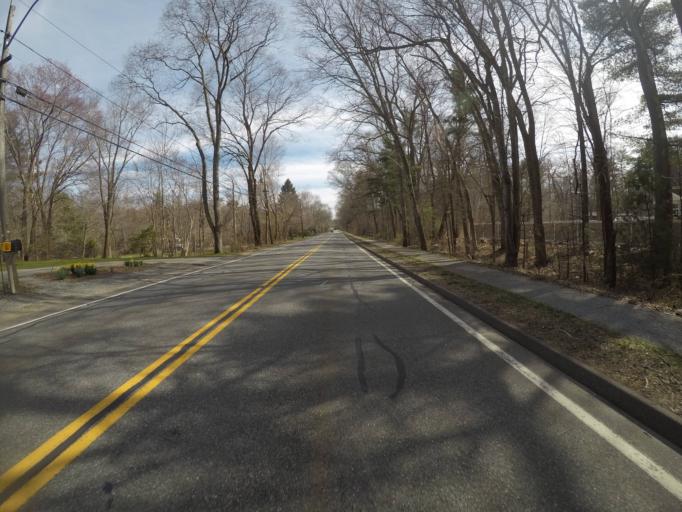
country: US
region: Massachusetts
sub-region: Plymouth County
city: West Bridgewater
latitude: 42.0311
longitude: -71.0666
